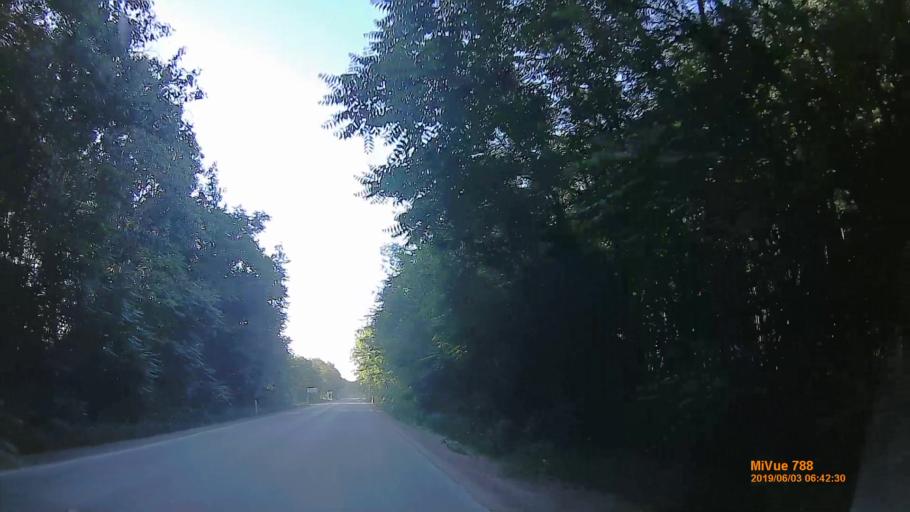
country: HU
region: Pest
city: Delegyhaza
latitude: 47.2657
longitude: 19.1157
